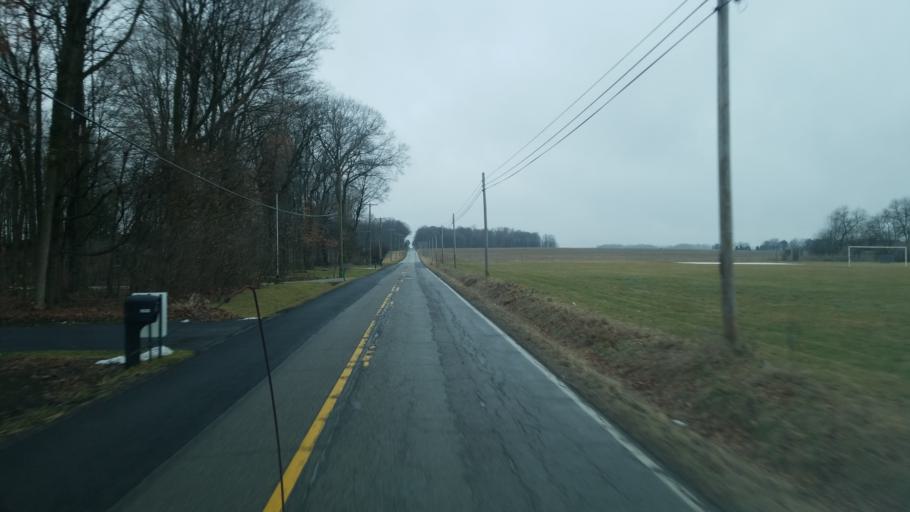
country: US
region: Ohio
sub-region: Wayne County
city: Orrville
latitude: 40.8591
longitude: -81.7917
